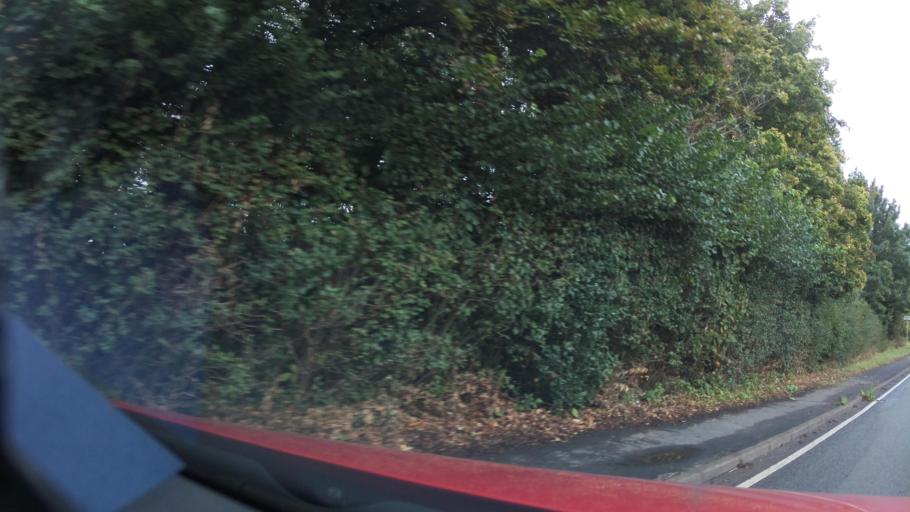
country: GB
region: England
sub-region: Worcestershire
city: Kidderminster
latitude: 52.3747
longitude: -2.2095
